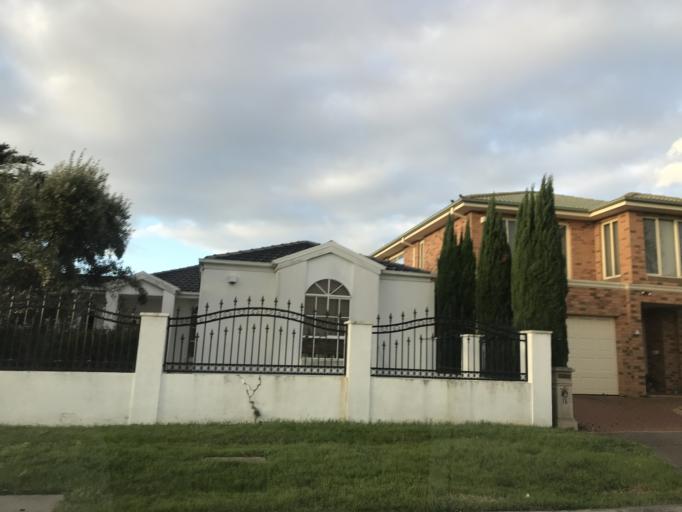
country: AU
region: Victoria
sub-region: Brimbank
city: Sunshine West
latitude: -37.7964
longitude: 144.7973
